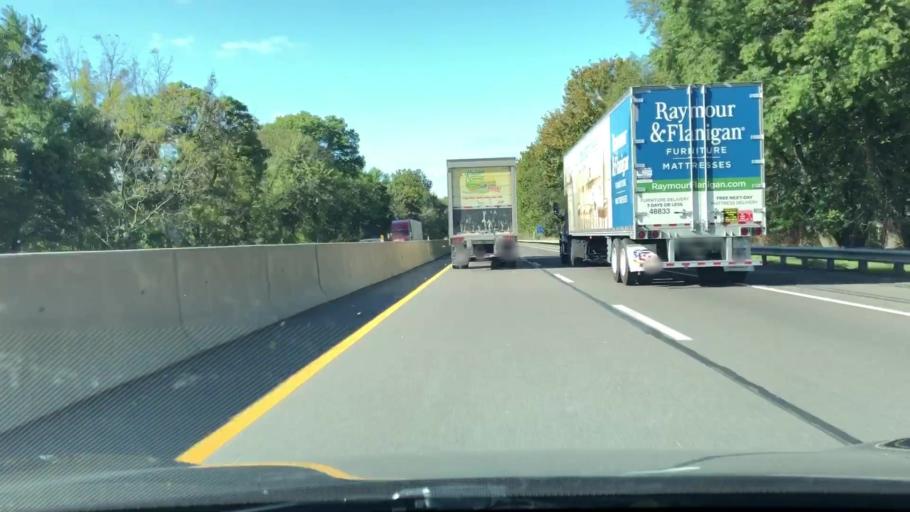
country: US
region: Pennsylvania
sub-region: Montgomery County
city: King of Prussia
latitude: 40.0893
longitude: -75.4185
